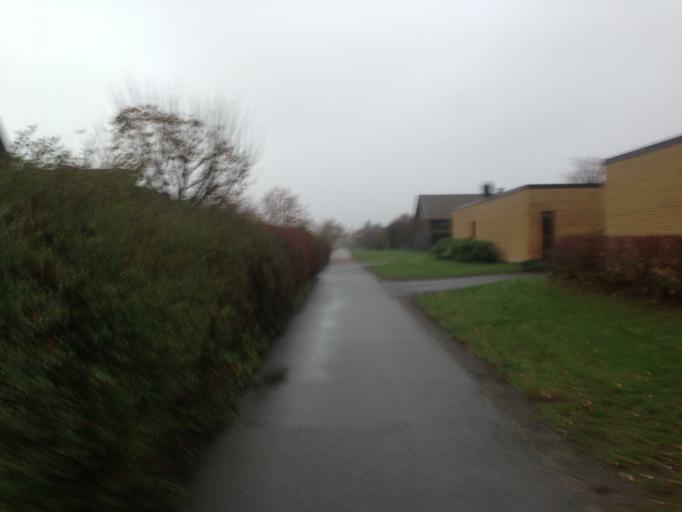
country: SE
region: Skane
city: Bjarred
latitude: 55.7243
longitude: 13.0074
